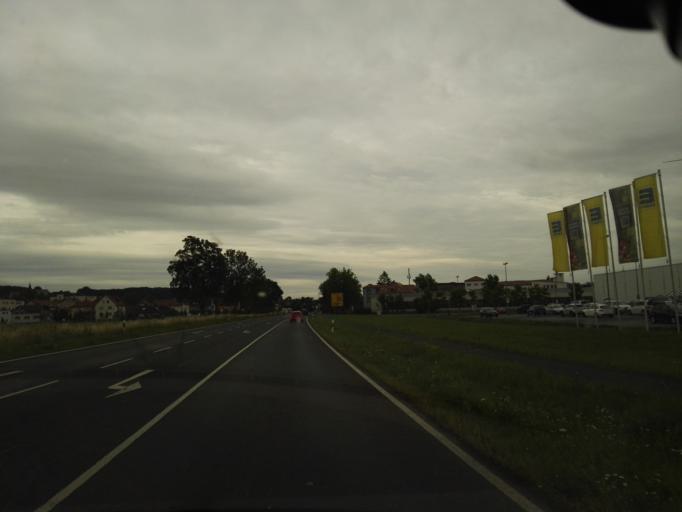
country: DE
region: Bavaria
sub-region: Upper Franconia
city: Burgkunstadt
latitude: 50.1415
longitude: 11.2422
